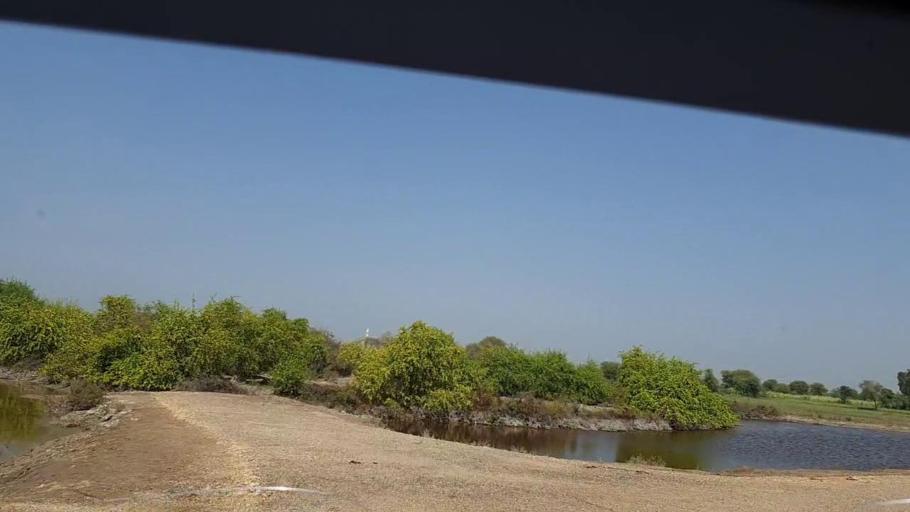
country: PK
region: Sindh
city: Rajo Khanani
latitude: 24.9364
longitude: 68.8797
